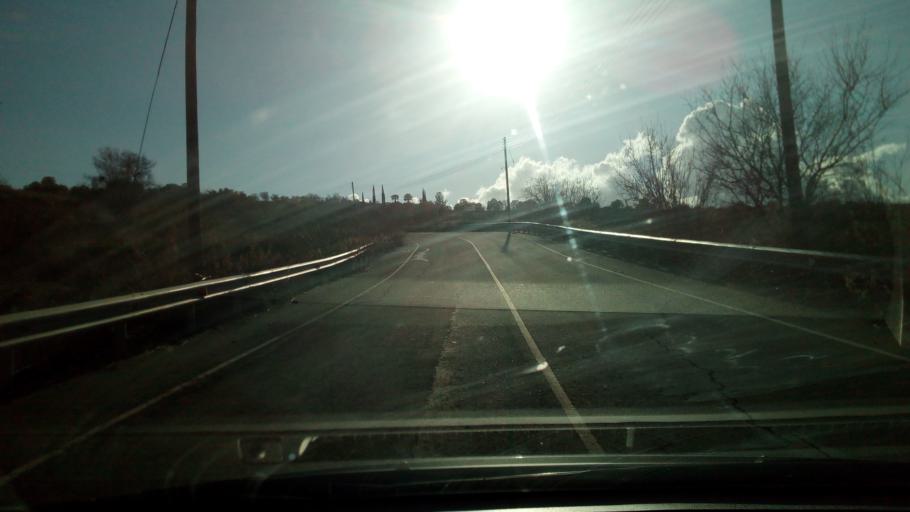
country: CY
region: Pafos
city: Tala
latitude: 34.9351
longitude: 32.5165
